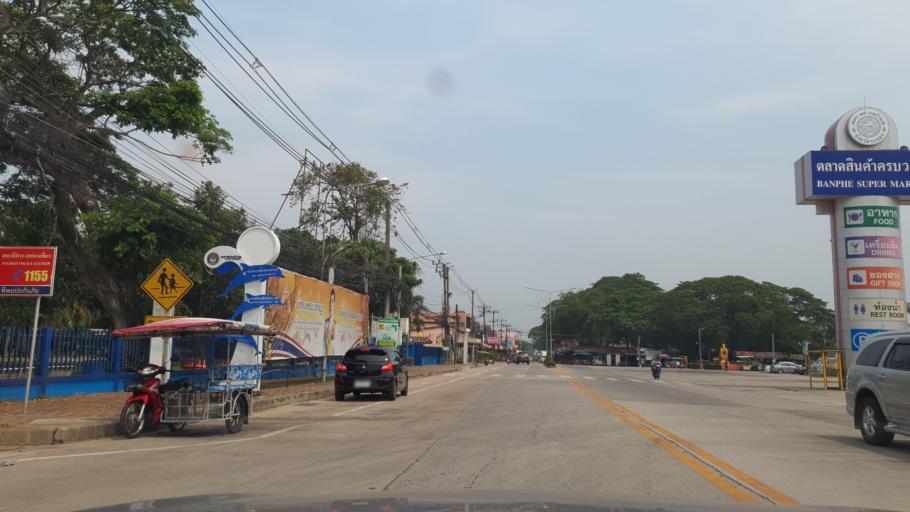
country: TH
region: Rayong
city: Rayong
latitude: 12.6229
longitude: 101.4265
